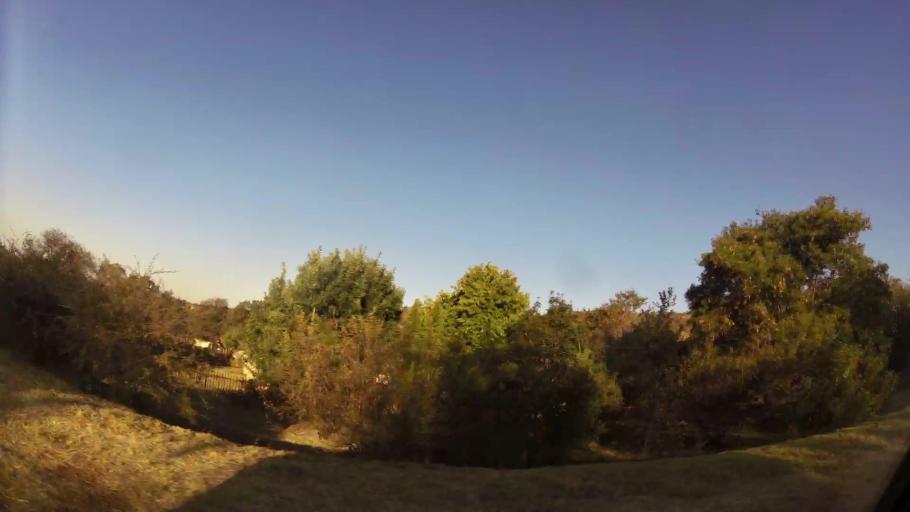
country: ZA
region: North-West
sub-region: Bojanala Platinum District Municipality
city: Rustenburg
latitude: -25.7158
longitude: 27.2390
